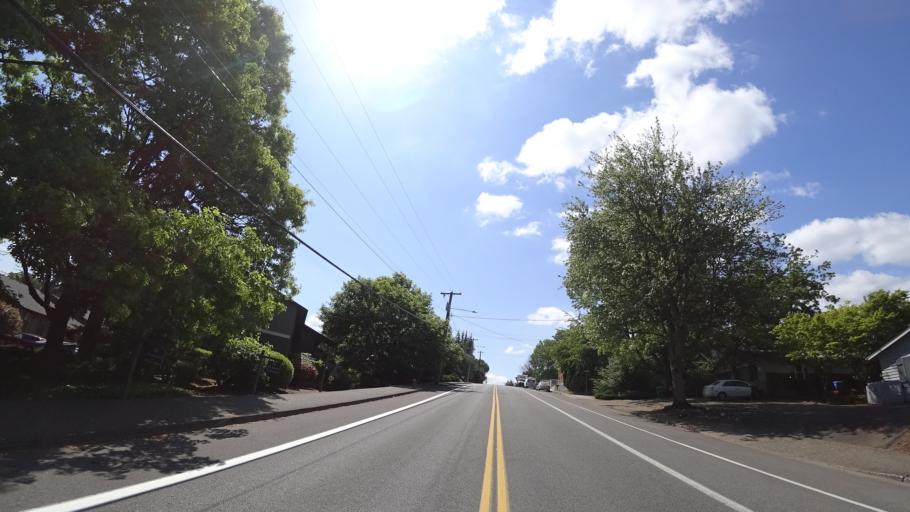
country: US
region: Oregon
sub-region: Multnomah County
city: Portland
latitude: 45.4760
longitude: -122.6981
